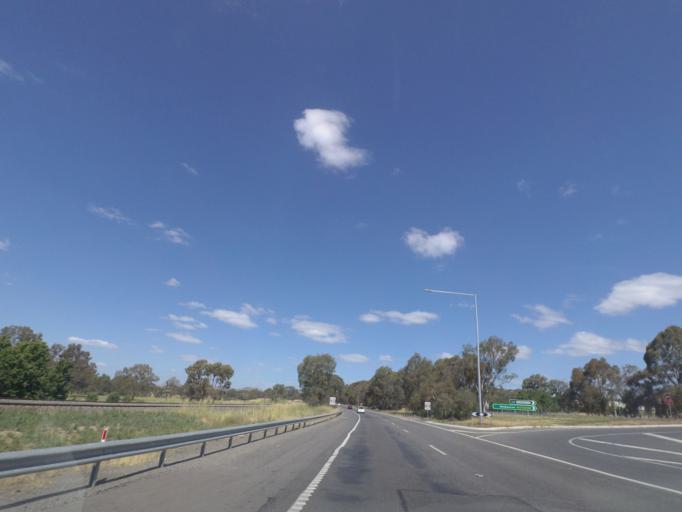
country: AU
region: Victoria
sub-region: Wodonga
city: Wodonga
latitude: -36.1030
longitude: 146.8269
